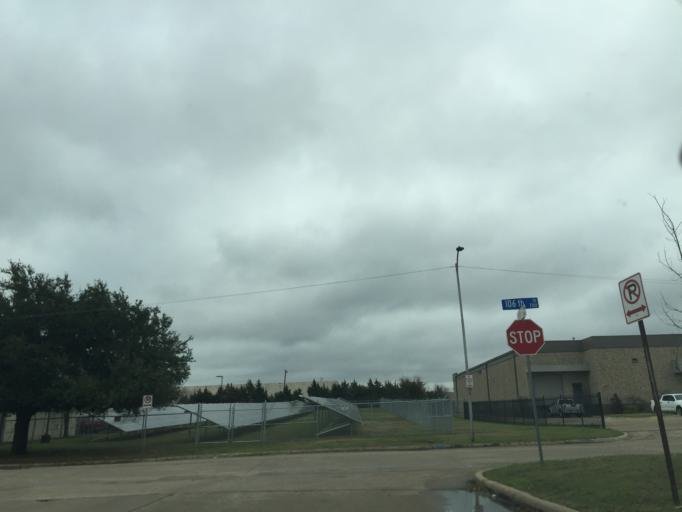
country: US
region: Texas
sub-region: Tarrant County
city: Arlington
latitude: 32.7550
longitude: -97.0603
